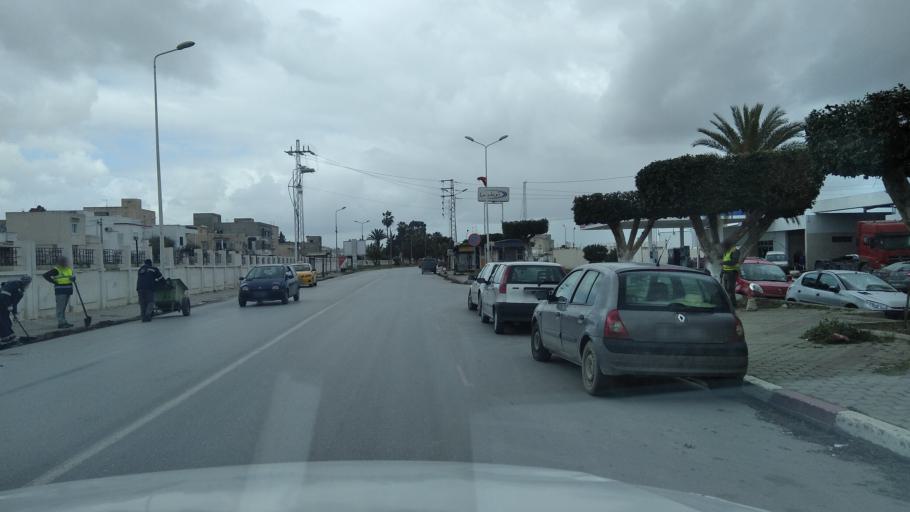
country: TN
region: Bin 'Arus
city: Ben Arous
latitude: 36.7568
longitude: 10.2194
